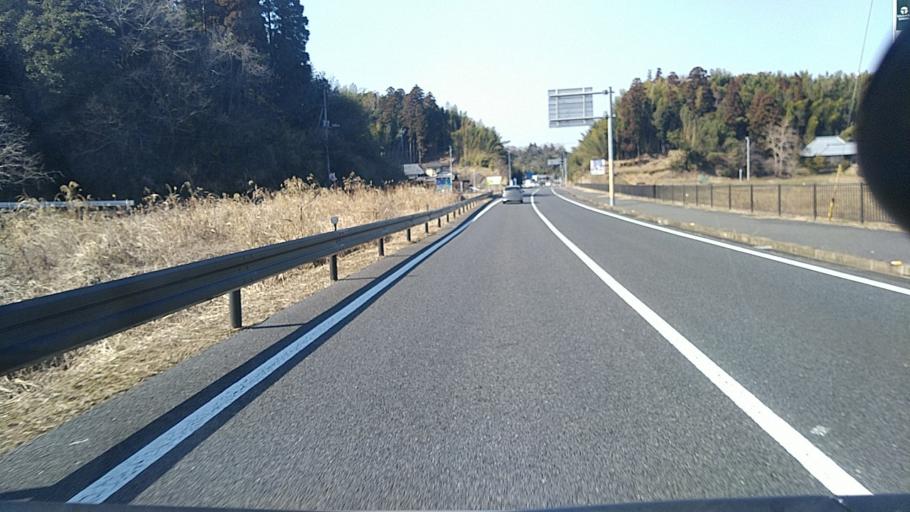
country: JP
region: Chiba
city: Mobara
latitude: 35.4025
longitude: 140.2417
